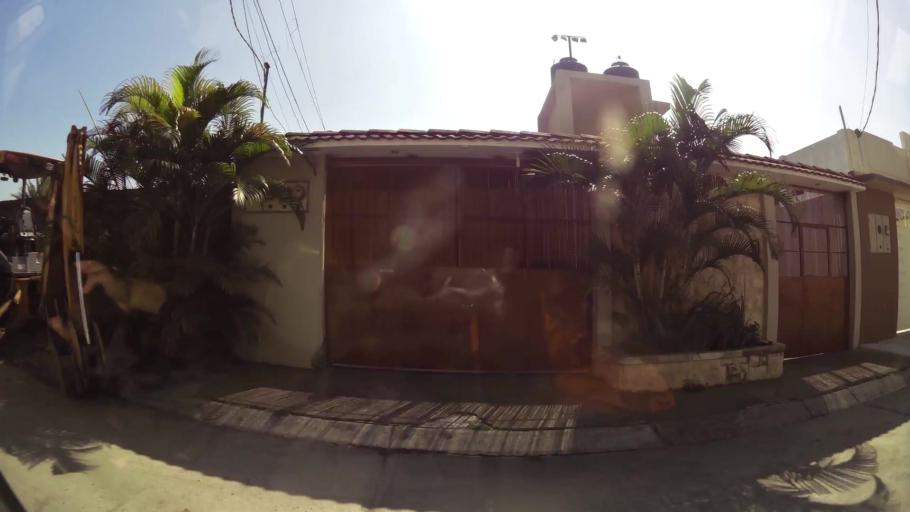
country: EC
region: Guayas
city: Guayaquil
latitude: -2.1815
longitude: -79.9141
